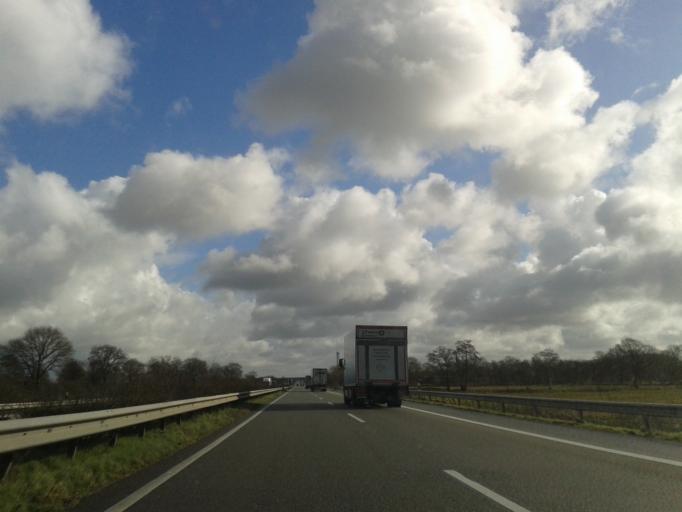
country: DE
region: Lower Saxony
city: Filsum
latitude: 53.2538
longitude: 7.6128
